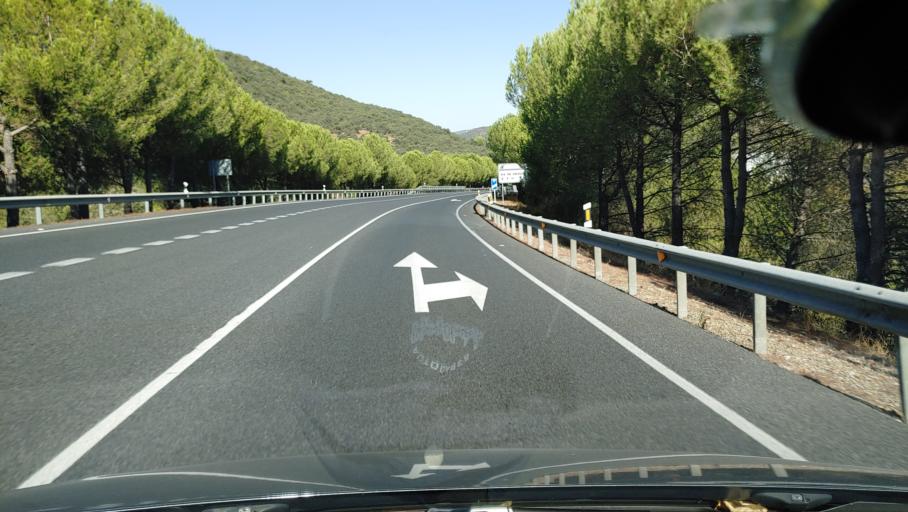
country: ES
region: Andalusia
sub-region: Province of Cordoba
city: Villaharta
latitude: 38.1208
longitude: -4.8952
